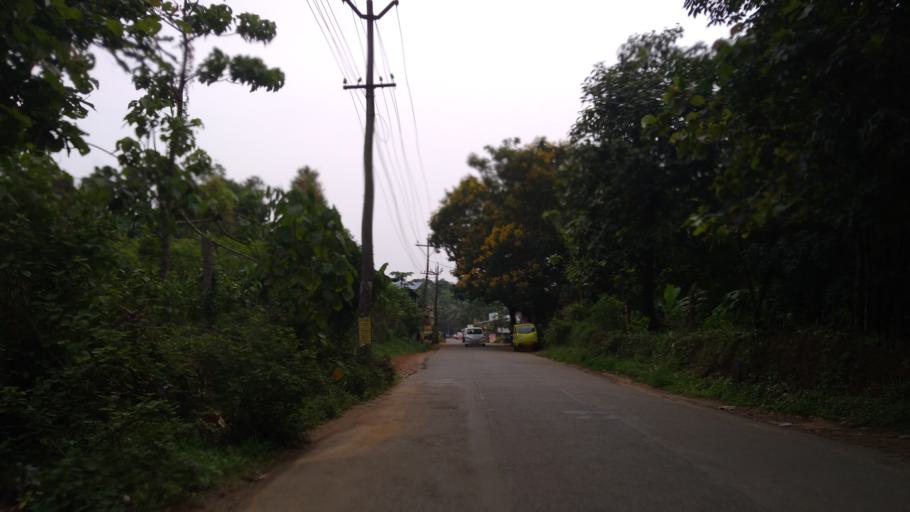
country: IN
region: Kerala
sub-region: Ernakulam
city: Kotamangalam
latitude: 10.1212
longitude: 76.5673
